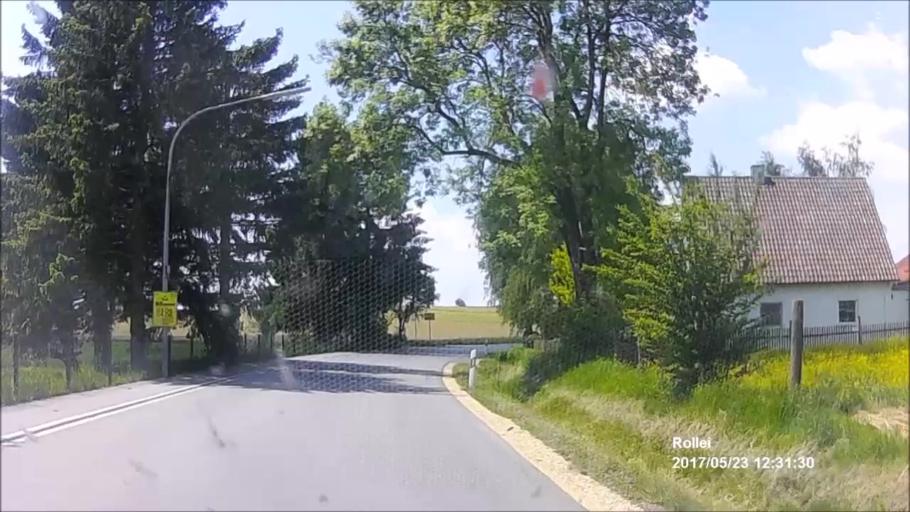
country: DE
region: Bavaria
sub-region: Lower Bavaria
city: Hohenthann
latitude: 48.6542
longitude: 12.1149
